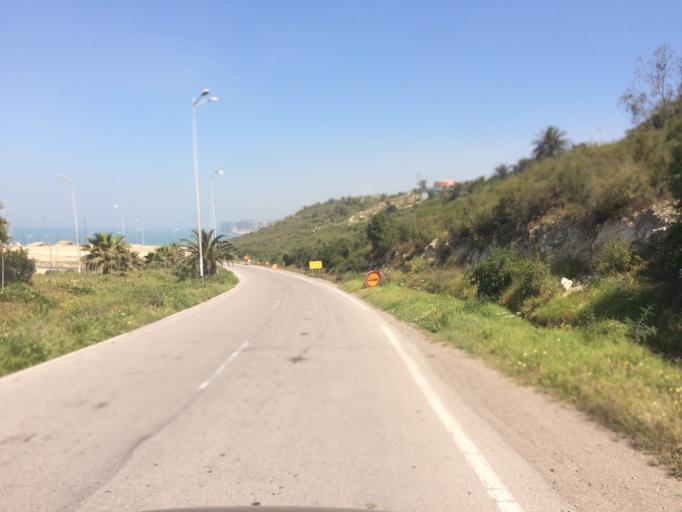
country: MA
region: Doukkala-Abda
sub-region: El-Jadida
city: Moulay Abdallah
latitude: 33.1362
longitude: -8.6105
